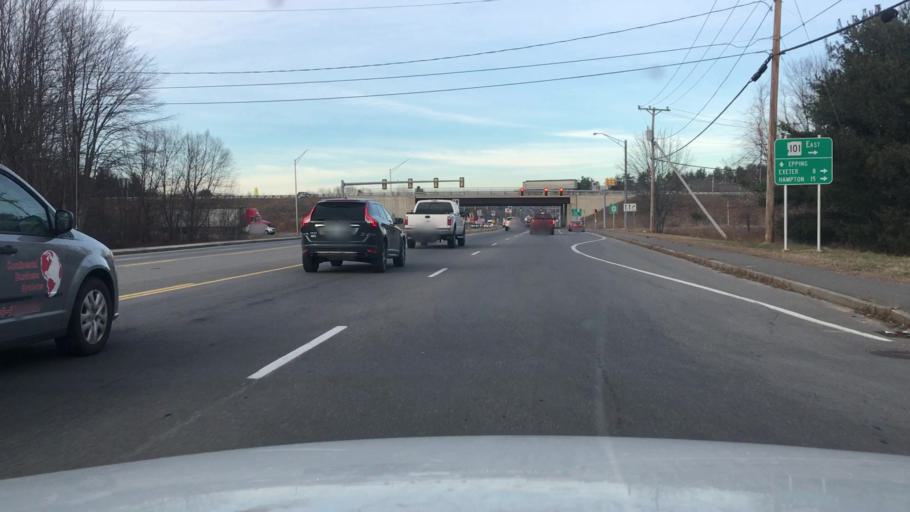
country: US
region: New Hampshire
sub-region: Rockingham County
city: Epping
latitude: 43.0246
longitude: -71.0737
